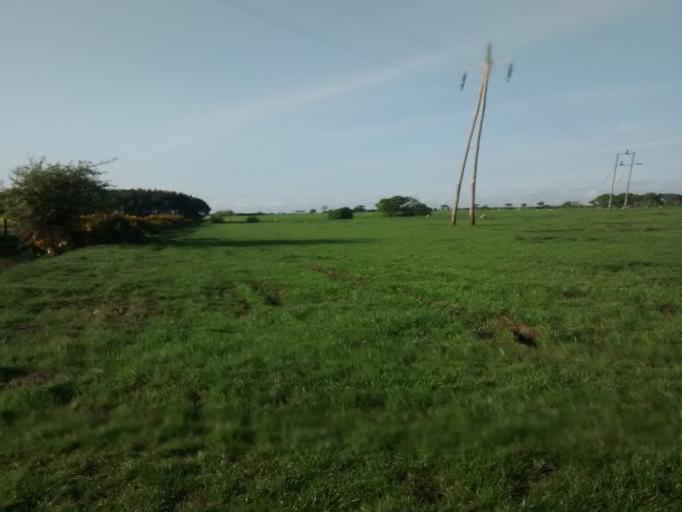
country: GB
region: England
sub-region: County Durham
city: West Cornforth
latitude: 54.7356
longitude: -1.5469
